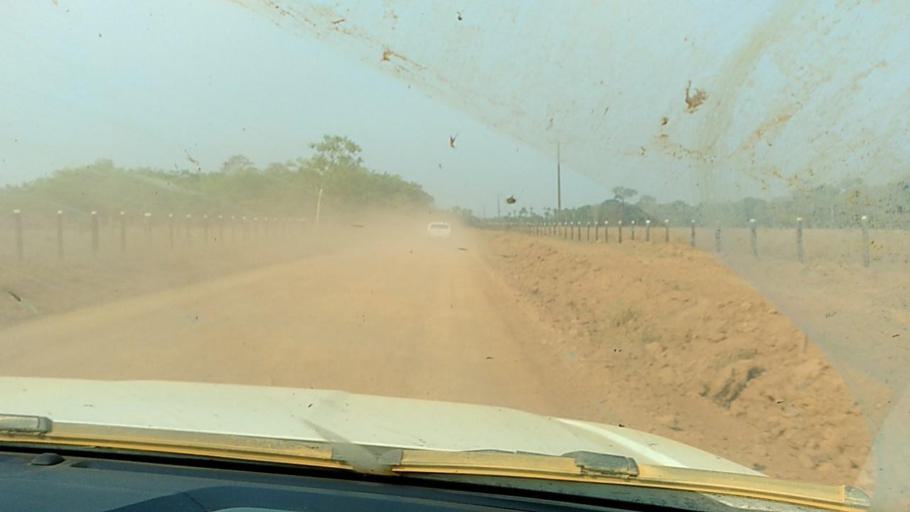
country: BR
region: Rondonia
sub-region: Porto Velho
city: Porto Velho
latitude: -8.7839
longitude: -64.0894
